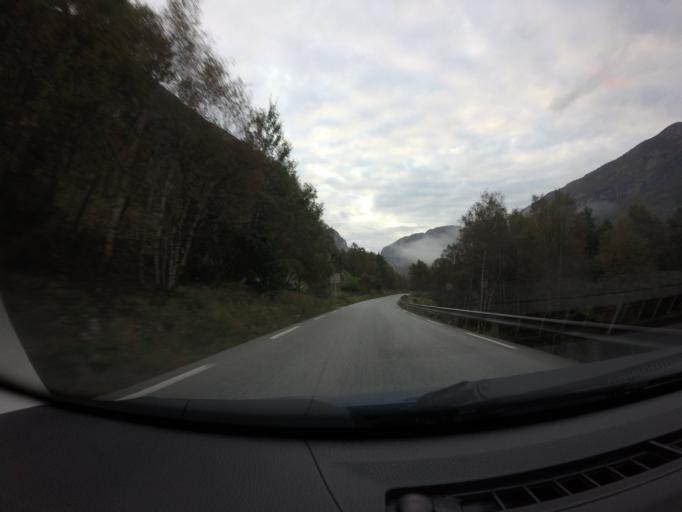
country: NO
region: Rogaland
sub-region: Forsand
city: Forsand
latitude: 58.8362
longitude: 6.0758
